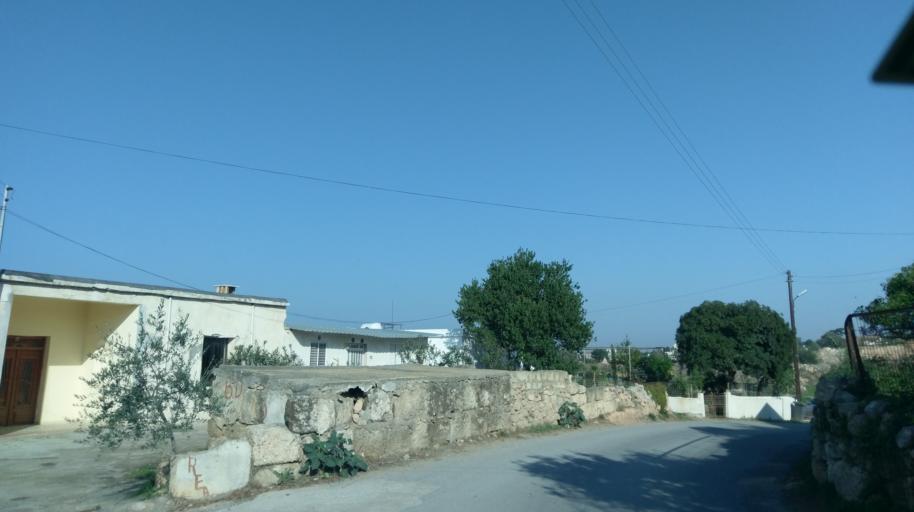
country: CY
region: Ammochostos
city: Leonarisso
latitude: 35.5336
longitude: 34.1910
